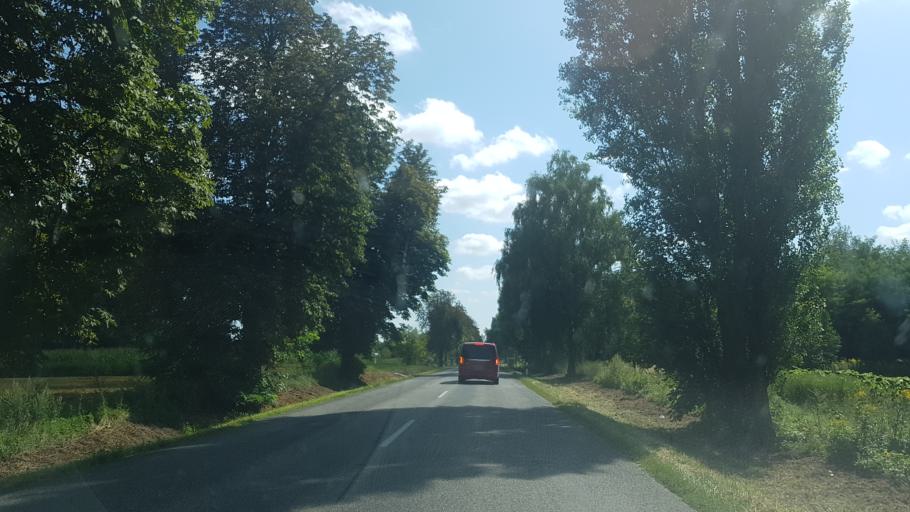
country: HU
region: Somogy
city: Marcali
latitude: 46.5150
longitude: 17.4246
